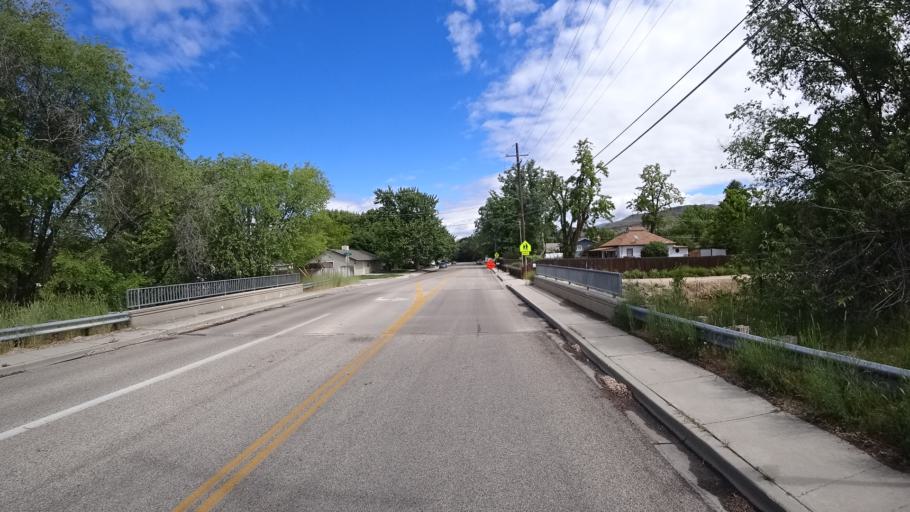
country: US
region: Idaho
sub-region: Ada County
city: Boise
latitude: 43.5743
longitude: -116.1635
